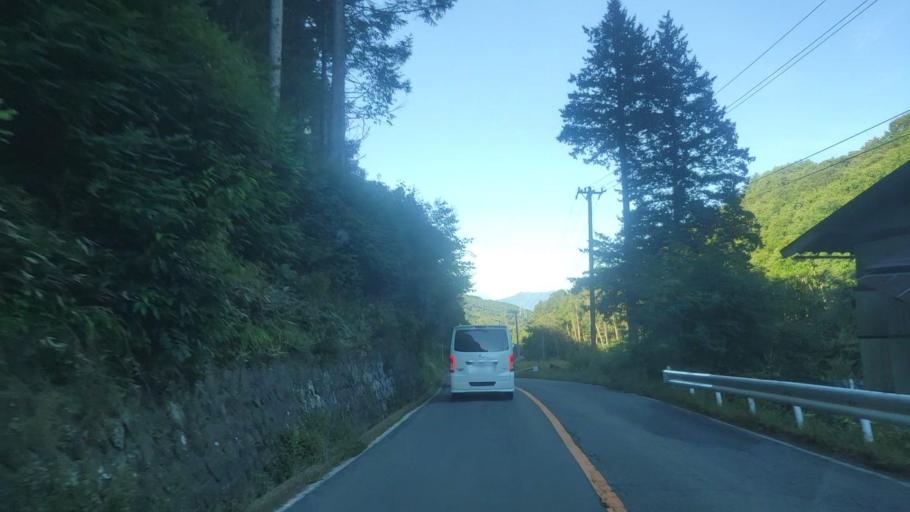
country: JP
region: Nagano
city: Kamimaruko
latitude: 36.2281
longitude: 138.2981
